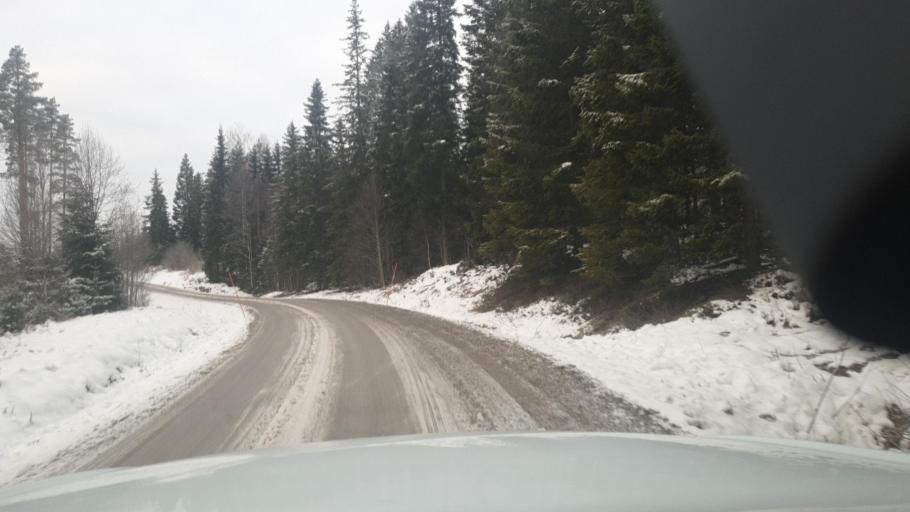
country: SE
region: Vaermland
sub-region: Sunne Kommun
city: Sunne
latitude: 59.8617
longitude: 12.8345
